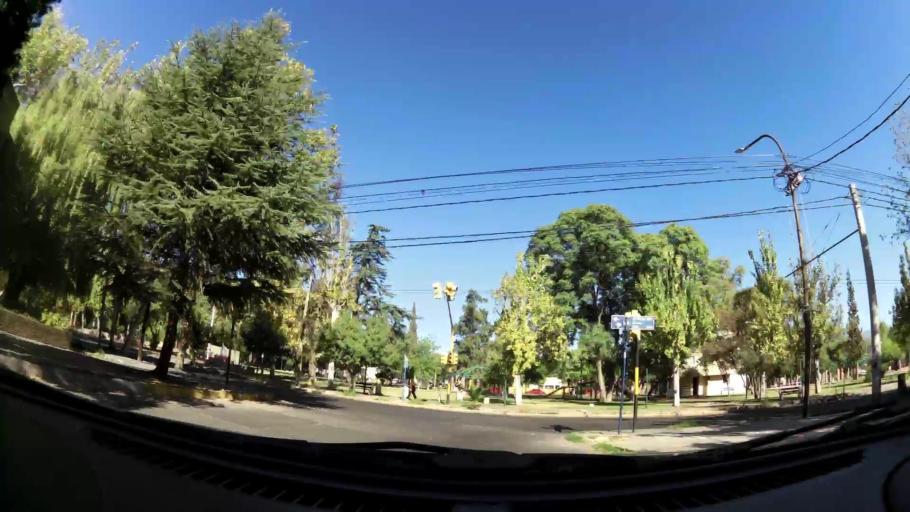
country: AR
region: Mendoza
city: Las Heras
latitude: -32.8707
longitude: -68.8583
